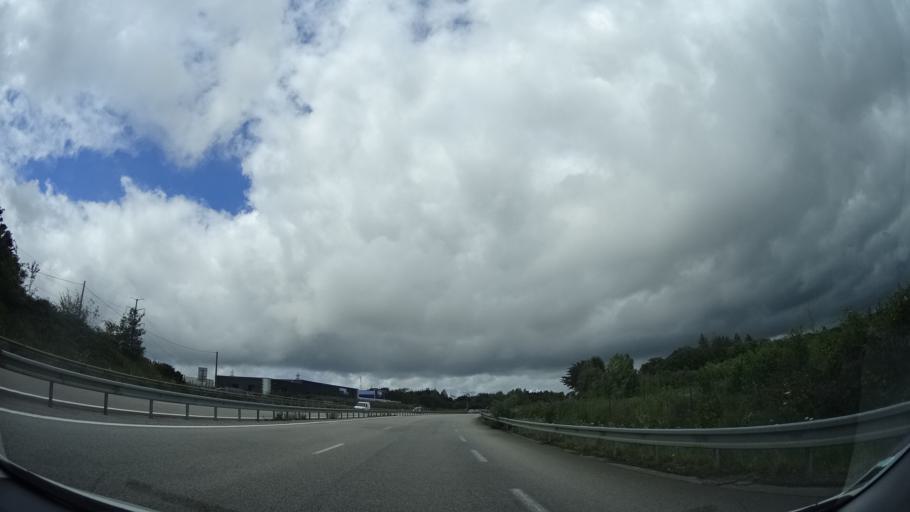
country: FR
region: Lower Normandy
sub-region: Departement de la Manche
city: La Glacerie
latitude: 49.5872
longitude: -1.5963
